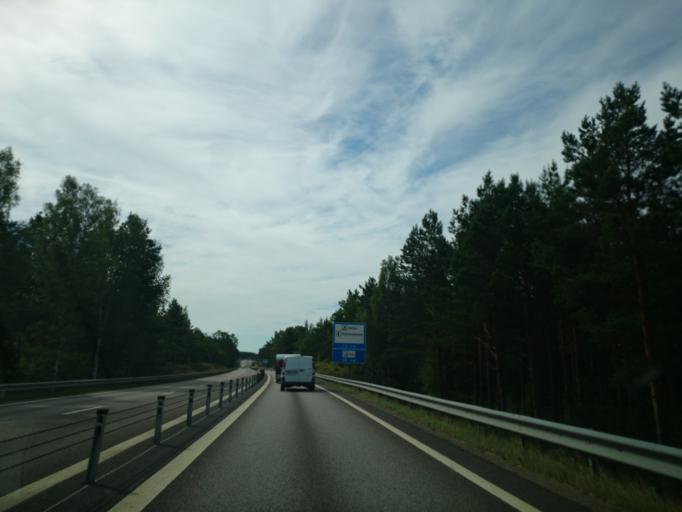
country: SE
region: Kalmar
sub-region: Oskarshamns Kommun
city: Oskarshamn
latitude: 57.3915
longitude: 16.4782
